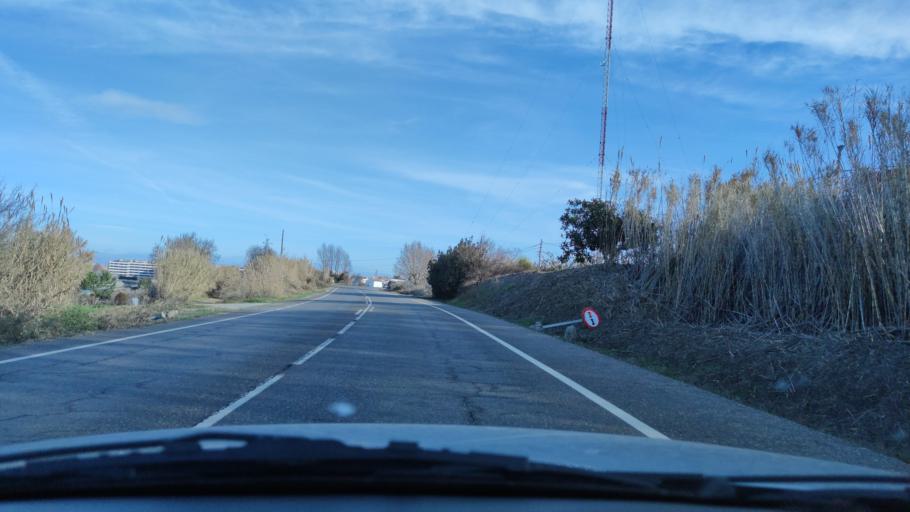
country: ES
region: Catalonia
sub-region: Provincia de Lleida
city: Lleida
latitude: 41.5938
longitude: 0.6345
